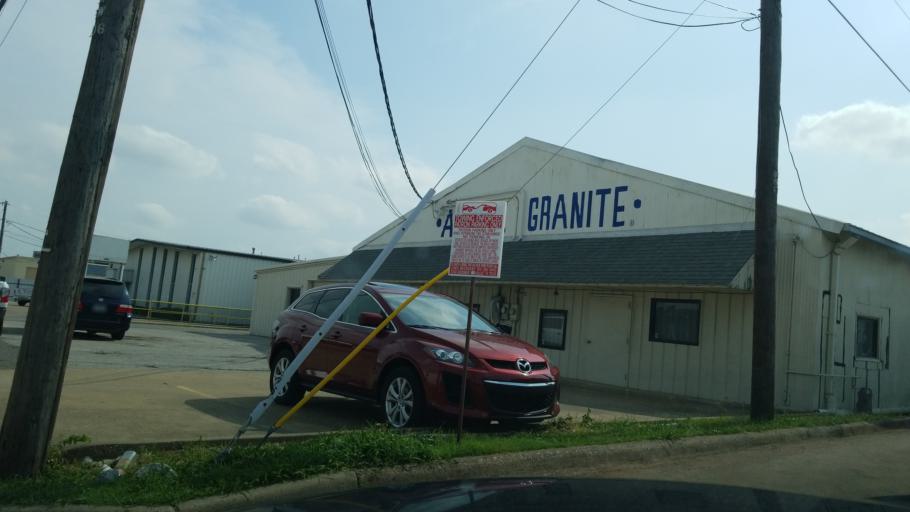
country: US
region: Texas
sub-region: Dallas County
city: Farmers Branch
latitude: 32.8985
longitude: -96.8815
